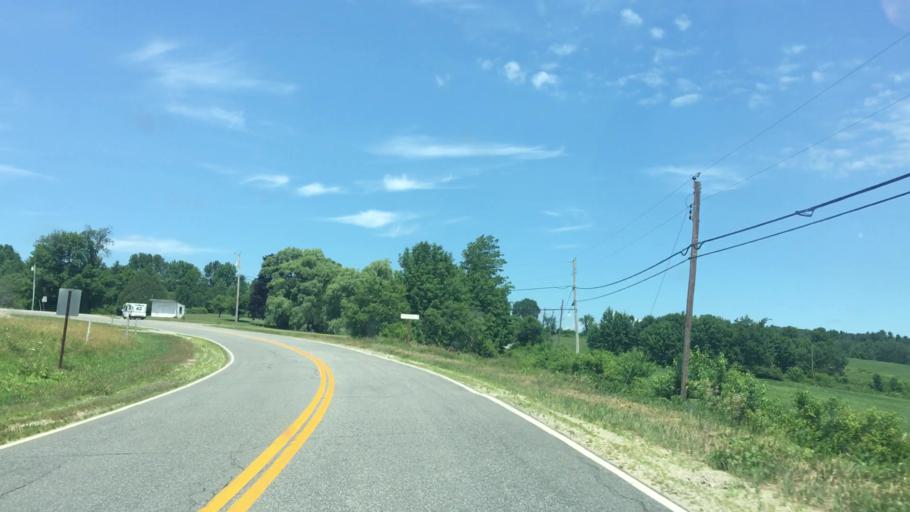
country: US
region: Maine
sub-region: Androscoggin County
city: Livermore
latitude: 44.3827
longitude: -70.2070
